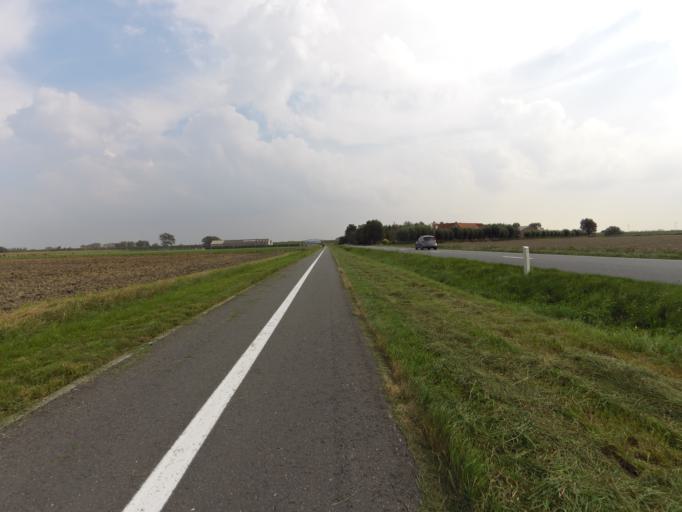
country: BE
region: Flanders
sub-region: Provincie West-Vlaanderen
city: Ostend
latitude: 51.1996
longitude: 2.9449
